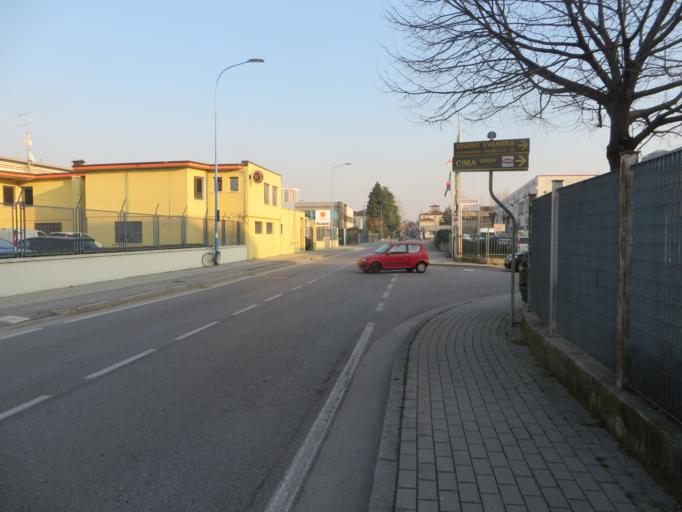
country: IT
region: Lombardy
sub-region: Provincia di Brescia
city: Brescia
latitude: 45.5258
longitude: 10.1937
